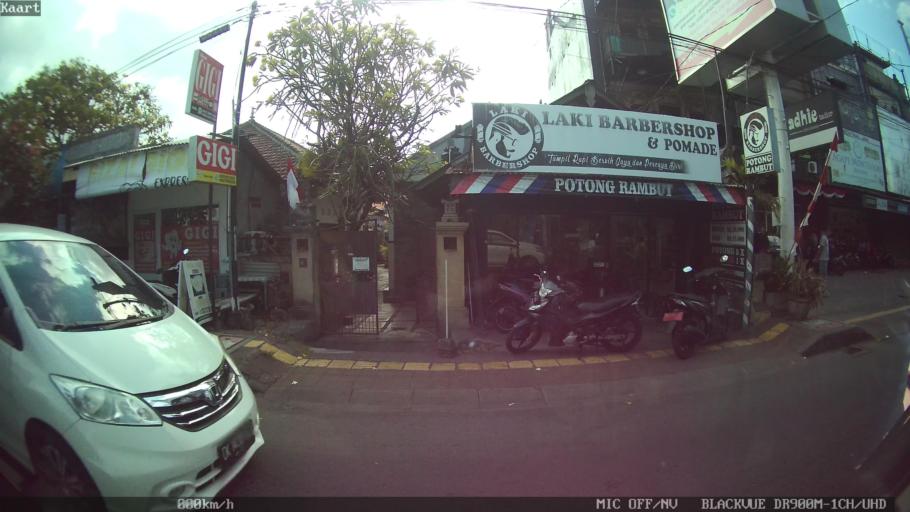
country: ID
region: Bali
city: Karyadharma
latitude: -8.6842
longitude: 115.2158
